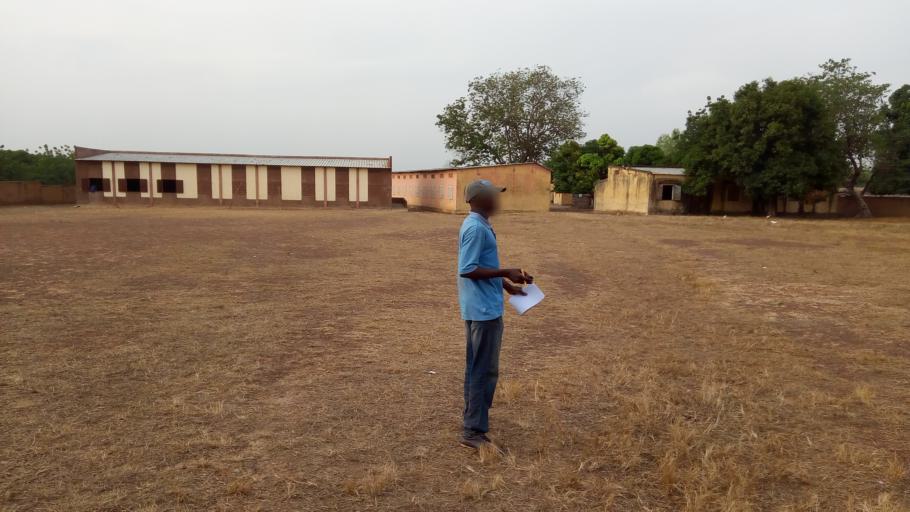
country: ML
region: Koulikoro
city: Kangaba
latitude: 11.6771
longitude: -8.6556
